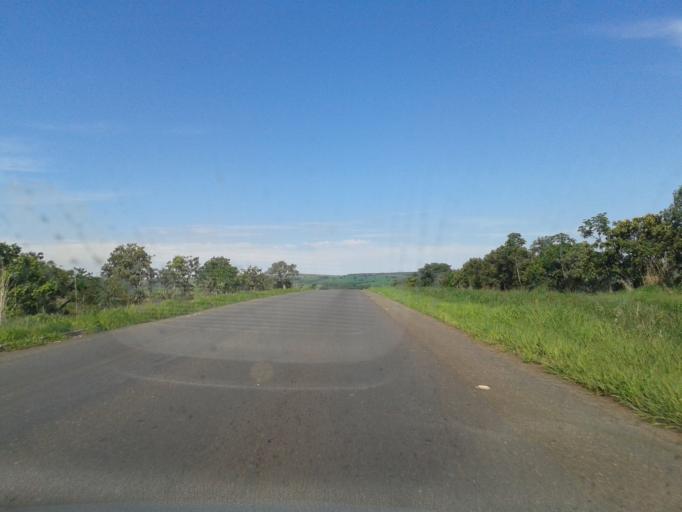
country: BR
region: Goias
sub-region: Bela Vista De Goias
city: Bela Vista de Goias
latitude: -17.1694
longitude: -48.7522
